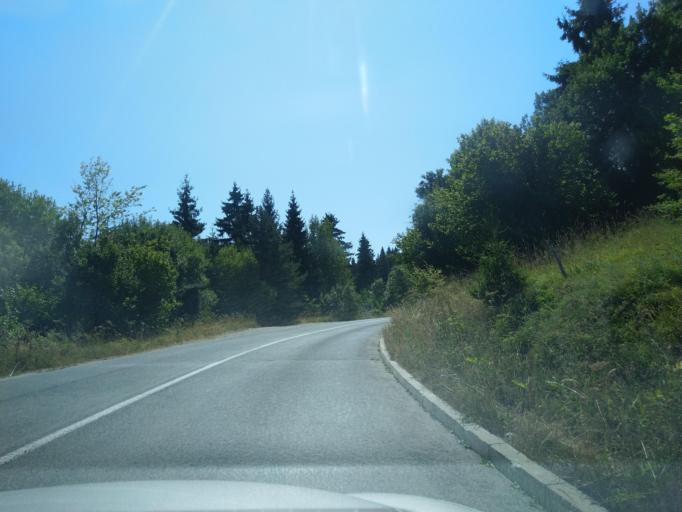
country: RS
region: Central Serbia
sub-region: Zlatiborski Okrug
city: Nova Varos
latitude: 43.4068
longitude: 19.8430
